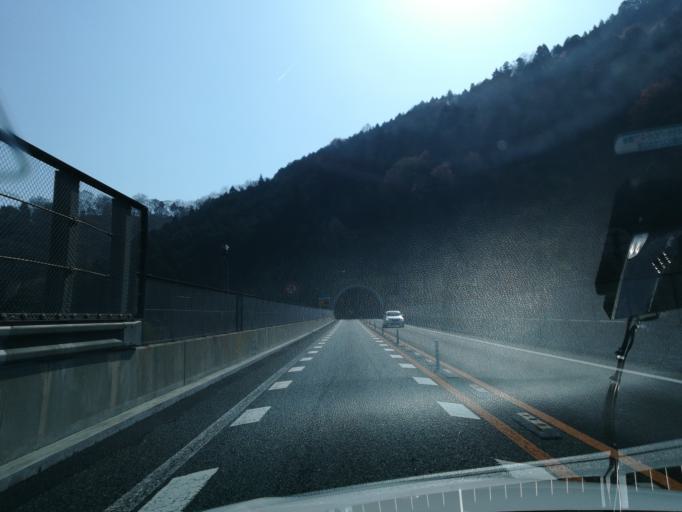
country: JP
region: Tokushima
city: Ikedacho
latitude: 34.0242
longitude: 133.7878
